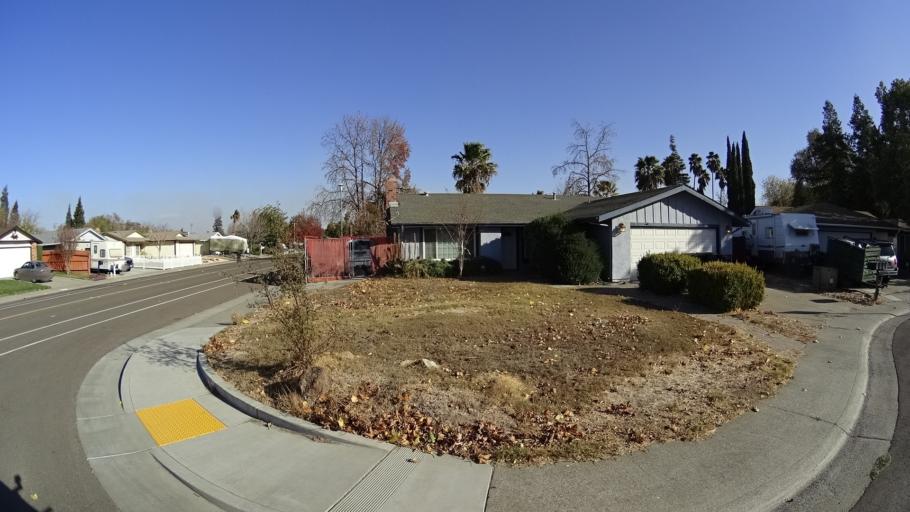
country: US
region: California
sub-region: Sacramento County
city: Antelope
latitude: 38.6989
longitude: -121.3146
